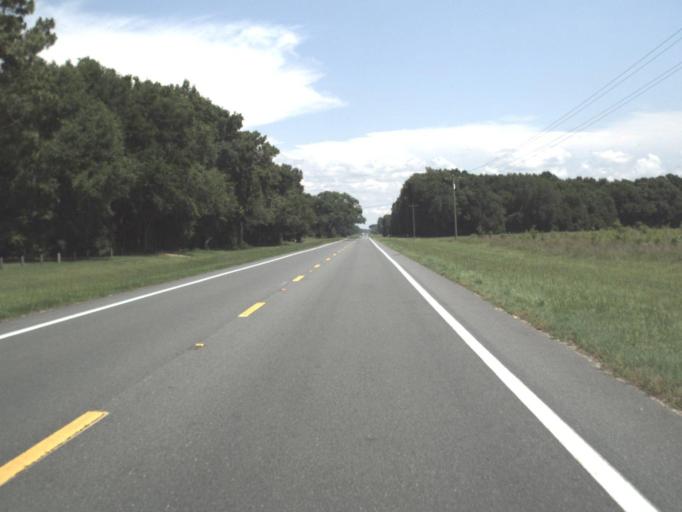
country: US
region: Florida
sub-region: Lafayette County
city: Mayo
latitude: 30.1059
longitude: -83.2470
